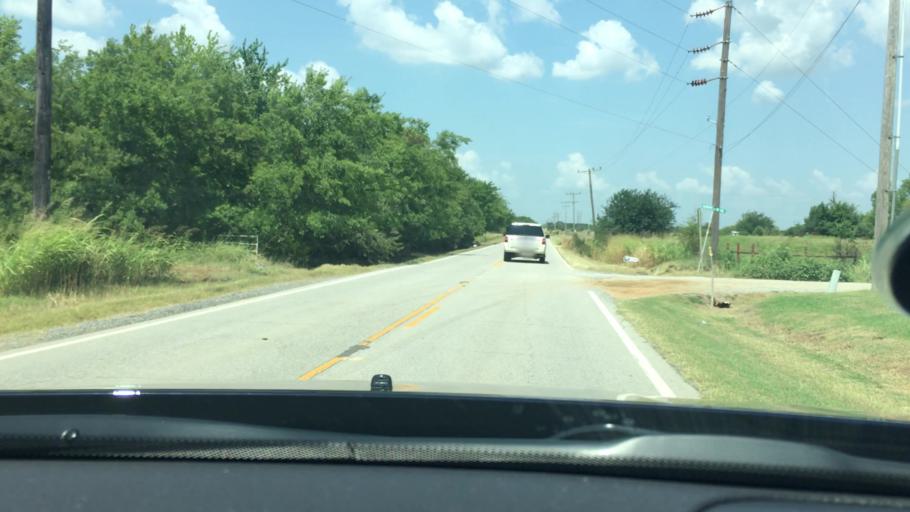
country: US
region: Oklahoma
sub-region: Bryan County
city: Durant
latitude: 34.0848
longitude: -96.4249
